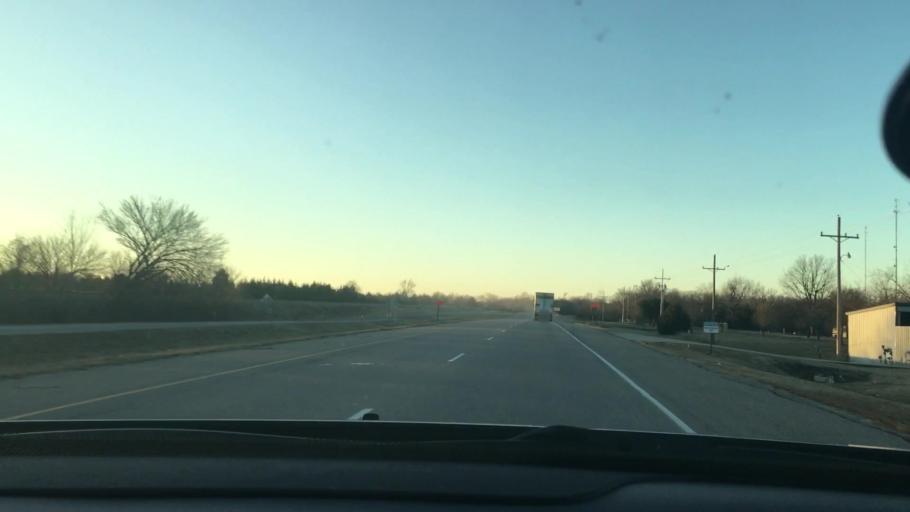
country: US
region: Oklahoma
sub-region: Pontotoc County
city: Ada
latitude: 34.7372
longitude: -96.7092
